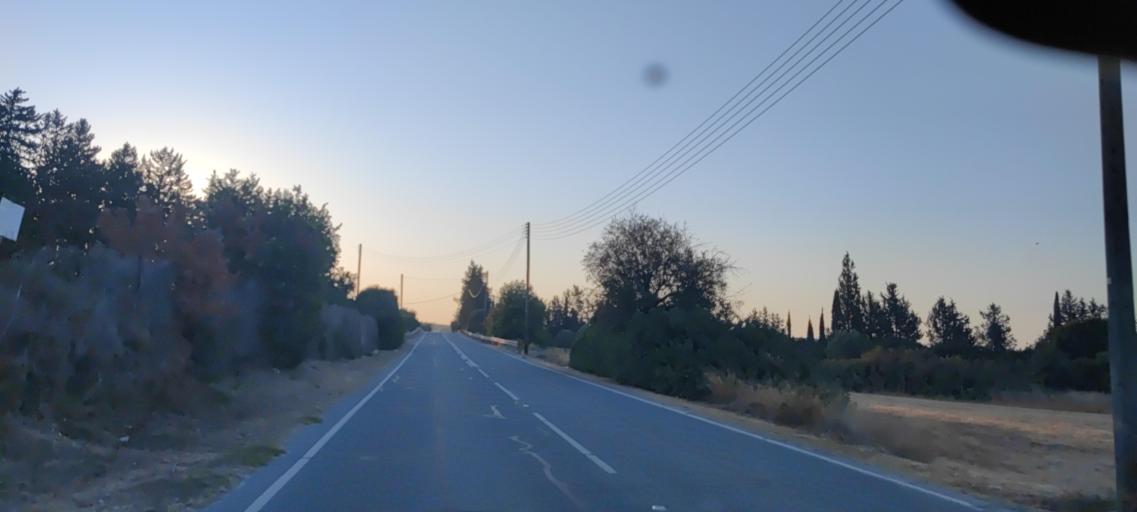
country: CY
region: Limassol
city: Pissouri
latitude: 34.6780
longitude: 32.7787
